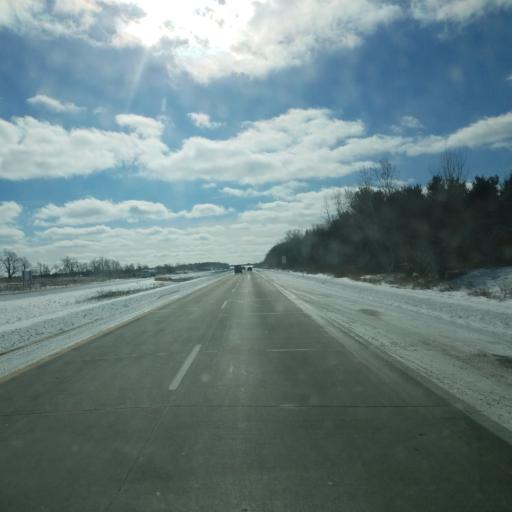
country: US
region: Michigan
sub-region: Clinton County
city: DeWitt
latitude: 42.8506
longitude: -84.5190
